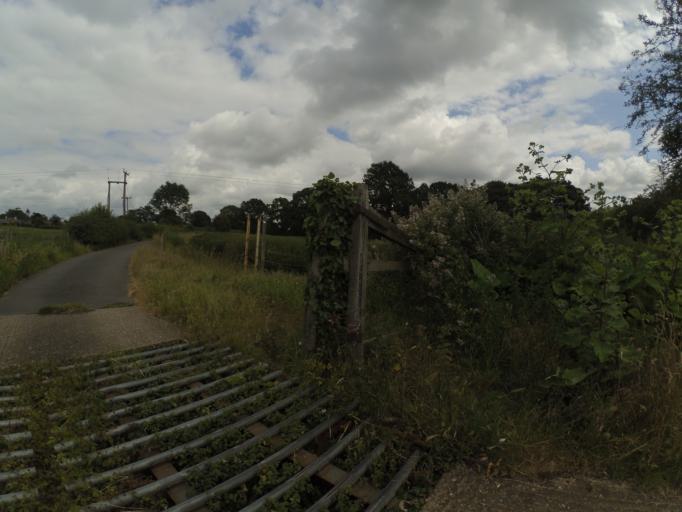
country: GB
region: England
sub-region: Warwickshire
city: Long Lawford
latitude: 52.3889
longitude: -1.2903
